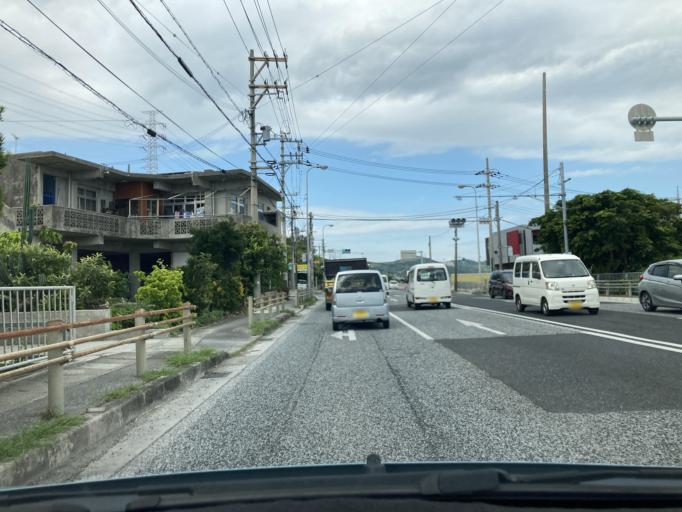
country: JP
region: Okinawa
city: Ginowan
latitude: 26.2548
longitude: 127.7847
